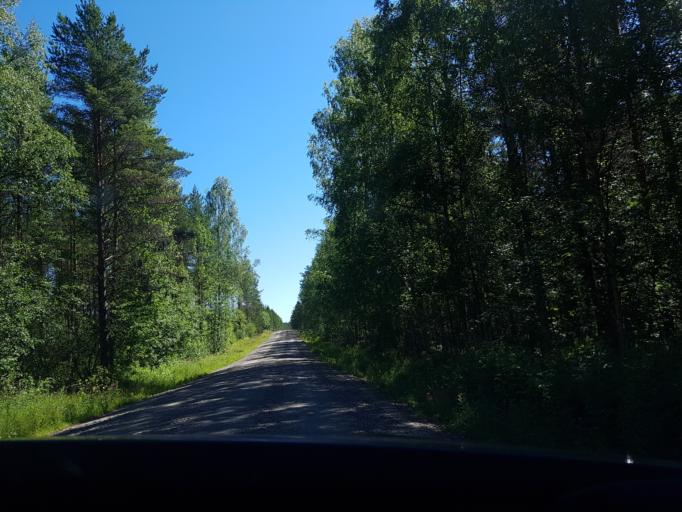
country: FI
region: Kainuu
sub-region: Kehys-Kainuu
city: Kuhmo
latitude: 64.1842
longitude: 29.5822
